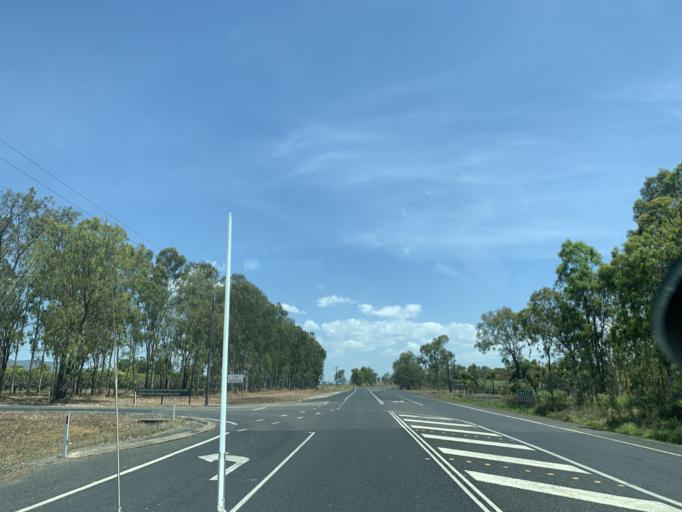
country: AU
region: Queensland
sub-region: Tablelands
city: Mareeba
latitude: -16.9777
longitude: 145.5325
